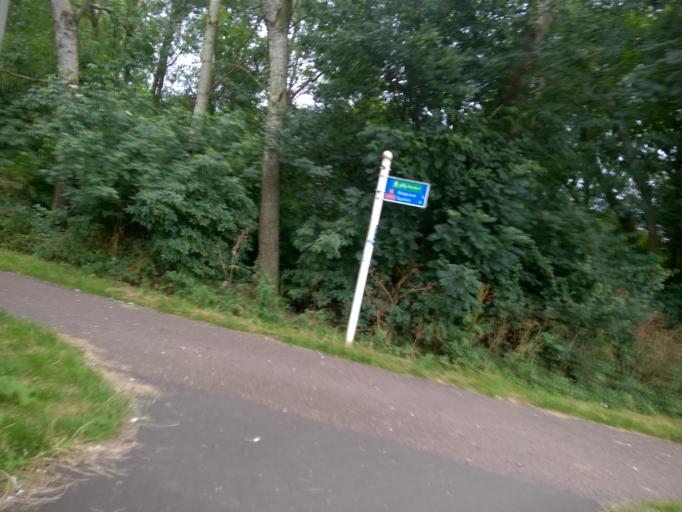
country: GB
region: England
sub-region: City of Leicester
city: Leicester
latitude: 52.6552
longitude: -1.1285
